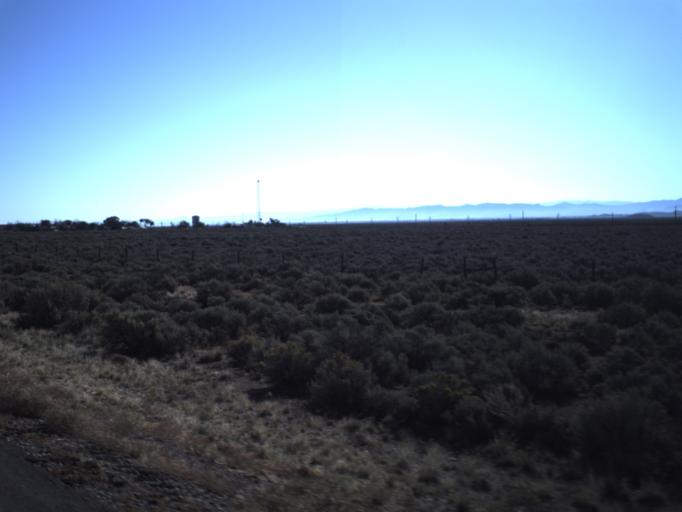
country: US
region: Utah
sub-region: Washington County
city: Enterprise
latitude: 37.7969
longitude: -113.9372
